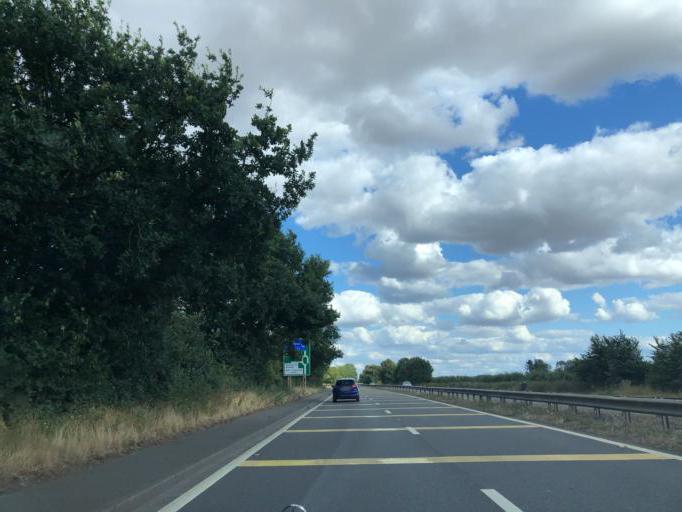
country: GB
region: England
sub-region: Warwickshire
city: Dunchurch
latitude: 52.3416
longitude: -1.3246
